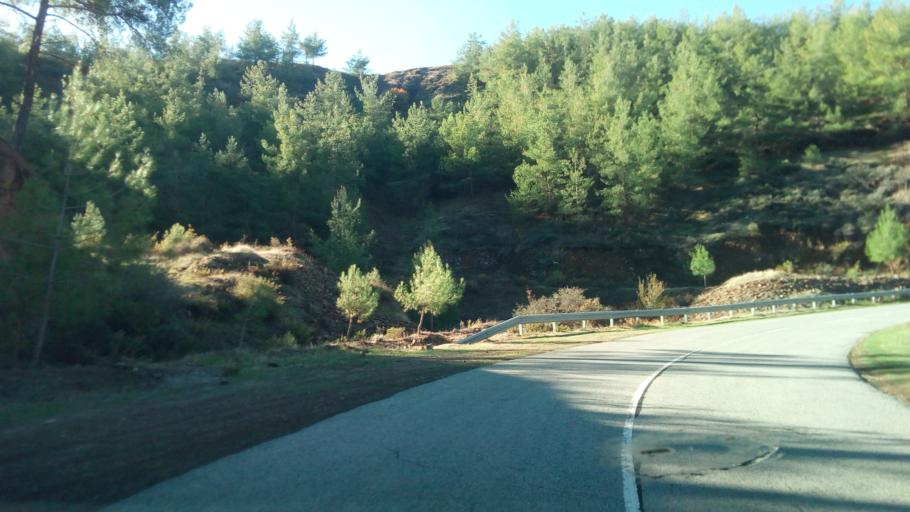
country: CY
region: Lefkosia
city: Lefka
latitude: 35.0857
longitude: 32.7870
